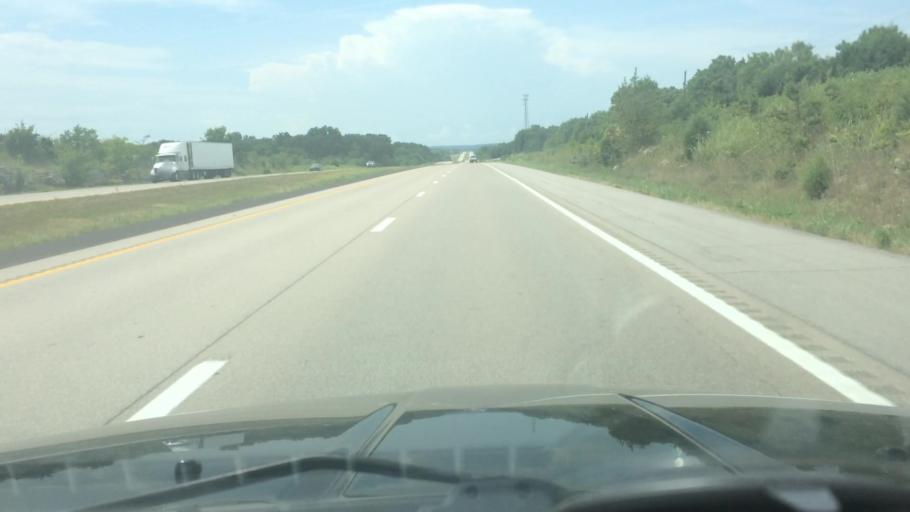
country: US
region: Missouri
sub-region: Polk County
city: Humansville
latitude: 37.7746
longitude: -93.5697
